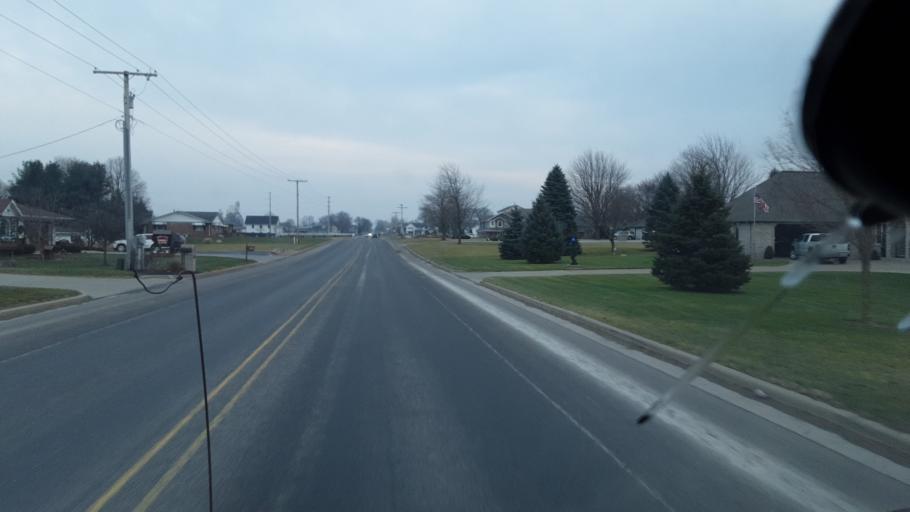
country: US
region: Indiana
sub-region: Elkhart County
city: Middlebury
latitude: 41.6762
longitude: -85.5927
